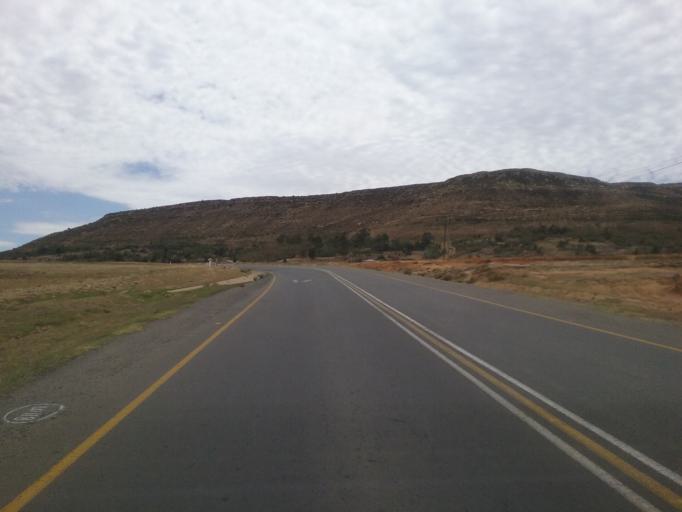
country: LS
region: Maseru
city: Nako
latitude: -29.6100
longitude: 27.5015
